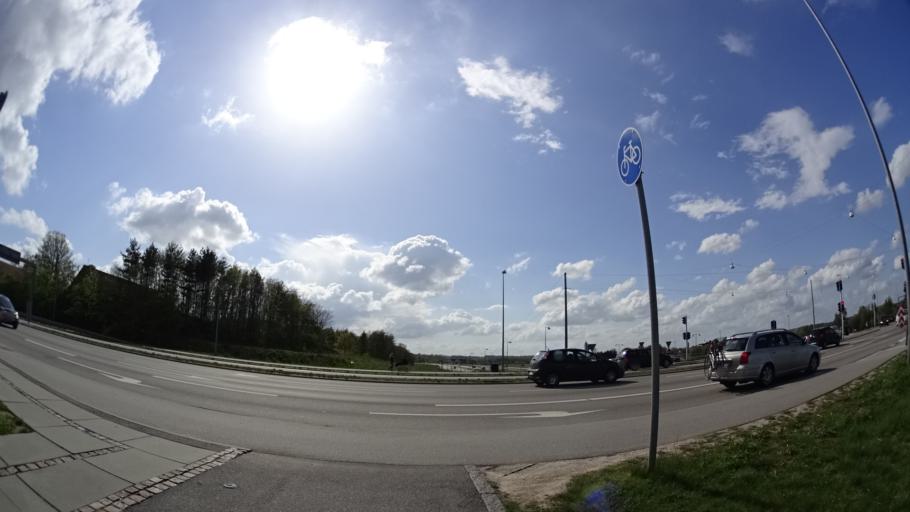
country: DK
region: Central Jutland
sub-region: Arhus Kommune
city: Stavtrup
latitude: 56.1354
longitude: 10.1568
